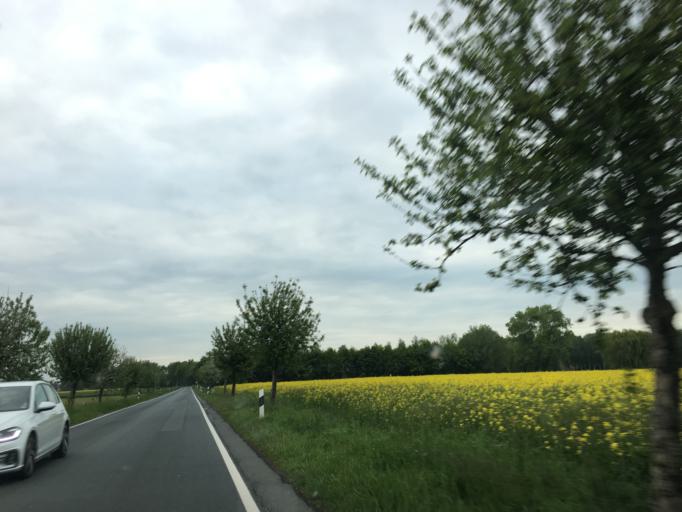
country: DE
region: Lower Saxony
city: Gross Munzel
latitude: 52.3819
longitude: 9.4447
